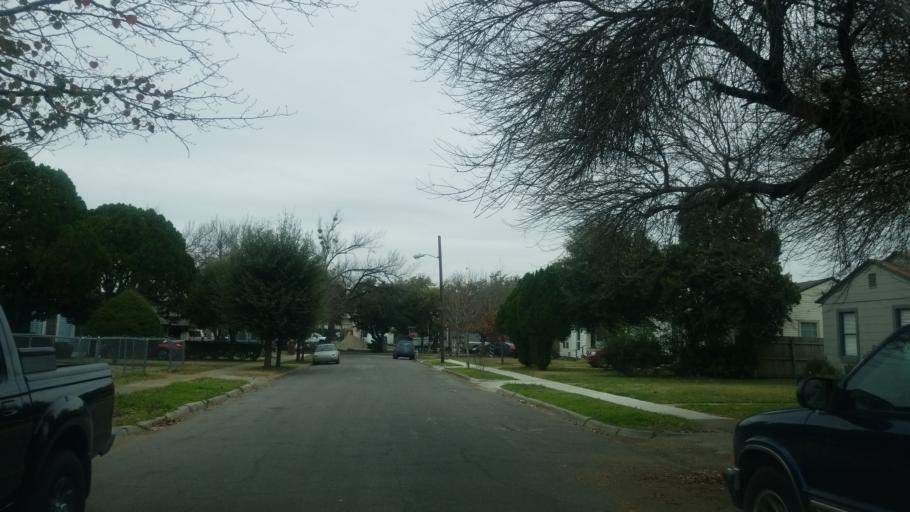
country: US
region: Texas
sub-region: Dallas County
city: Highland Park
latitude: 32.8228
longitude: -96.8317
